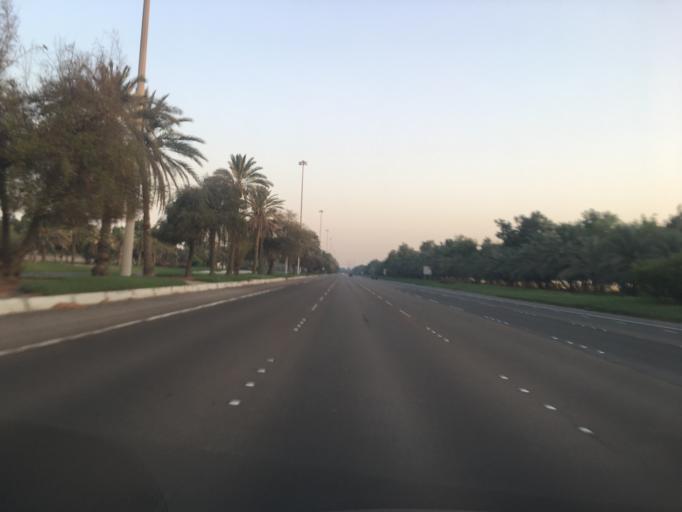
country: AE
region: Abu Dhabi
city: Abu Dhabi
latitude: 24.3945
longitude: 54.5352
